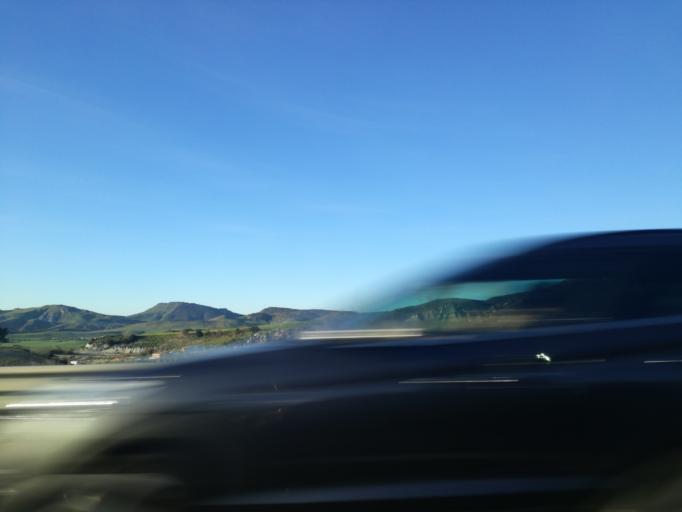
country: IT
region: Sicily
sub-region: Catania
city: San Michele di Ganzaria
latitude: 37.2157
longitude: 14.4126
